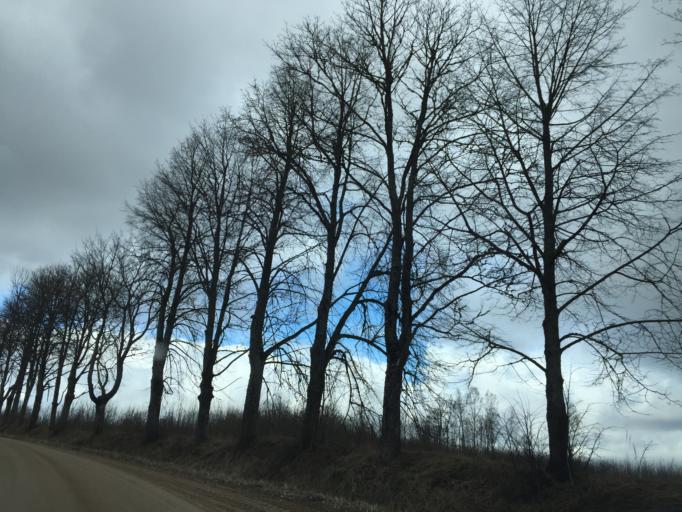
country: LV
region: Ilukste
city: Ilukste
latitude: 56.0842
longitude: 26.0308
